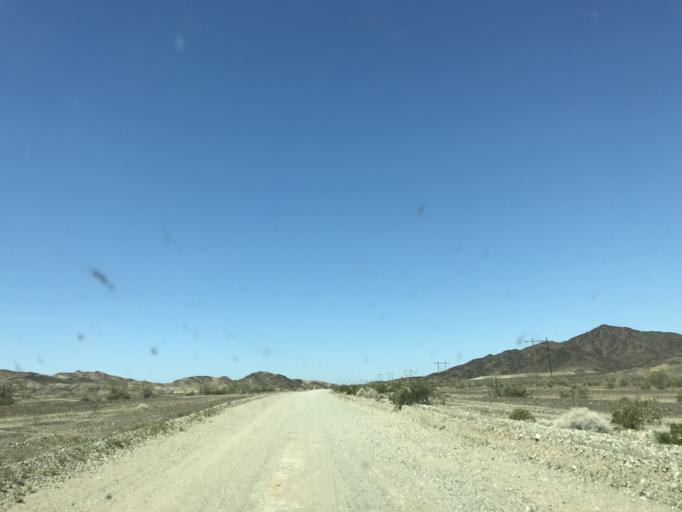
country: US
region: California
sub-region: Riverside County
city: Mesa Verde
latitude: 33.4934
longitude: -114.8162
